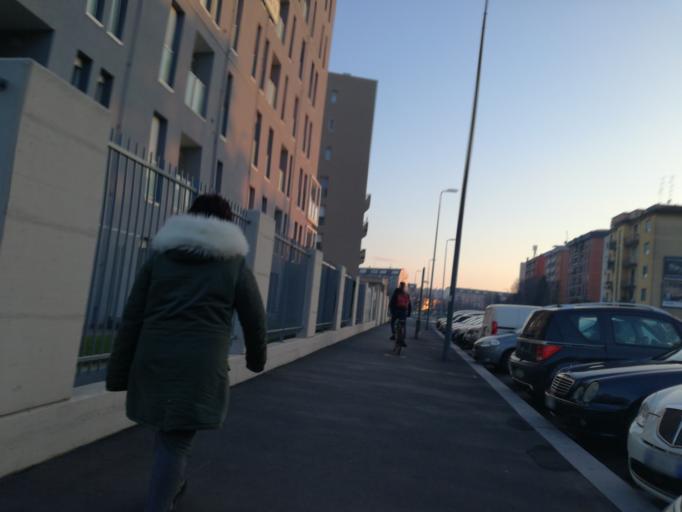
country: IT
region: Lombardy
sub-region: Citta metropolitana di Milano
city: Romano Banco
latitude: 45.4347
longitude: 9.1546
